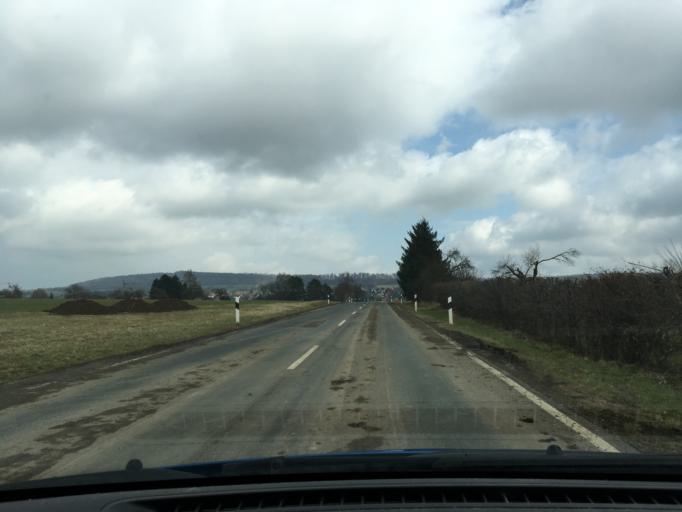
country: DE
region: Lower Saxony
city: Dransfeld
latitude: 51.5011
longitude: 9.7445
